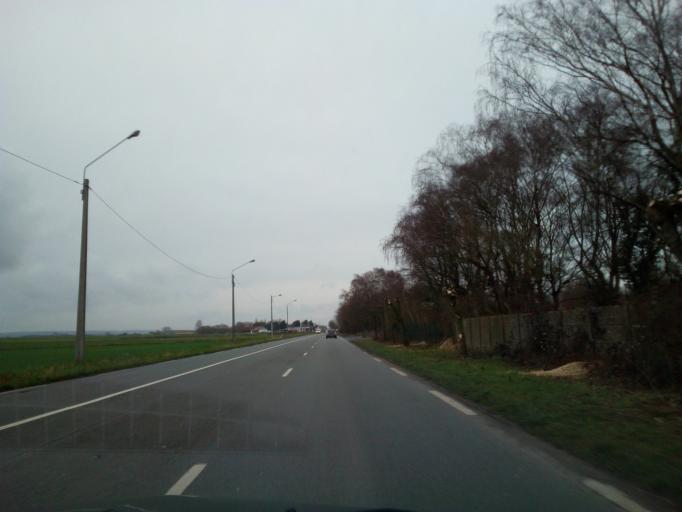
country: FR
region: Nord-Pas-de-Calais
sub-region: Departement du Pas-de-Calais
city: Auchy-les-Mines
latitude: 50.5163
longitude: 2.7705
